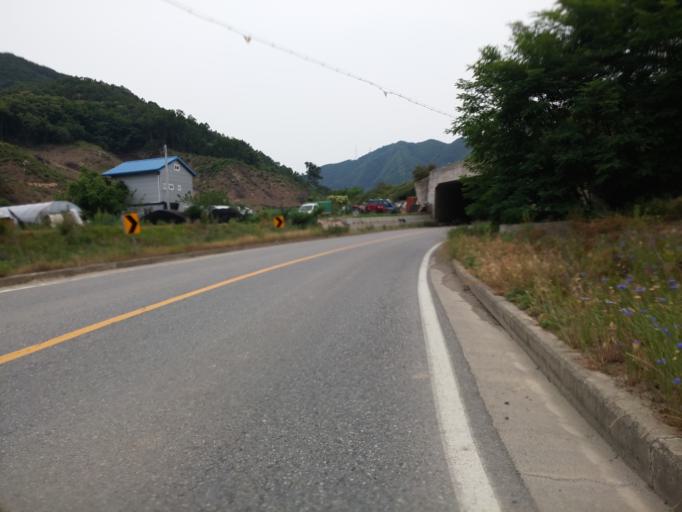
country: KR
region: Chungcheongbuk-do
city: Okcheon
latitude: 36.2605
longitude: 127.5187
